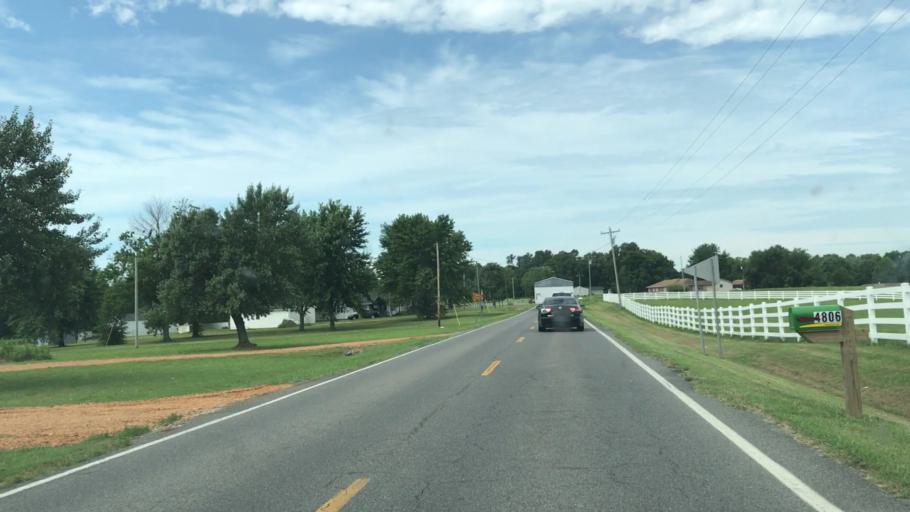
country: US
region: Kentucky
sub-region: Graves County
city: Mayfield
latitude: 36.8289
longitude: -88.5904
